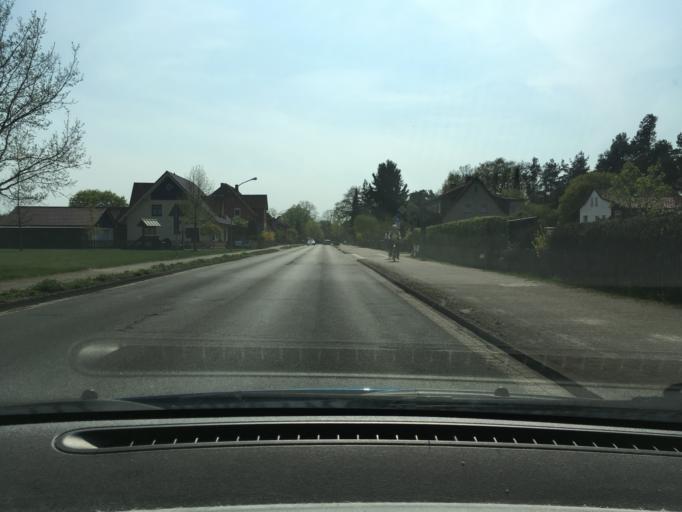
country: DE
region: Lower Saxony
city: Fassberg
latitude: 52.8785
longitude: 10.1243
